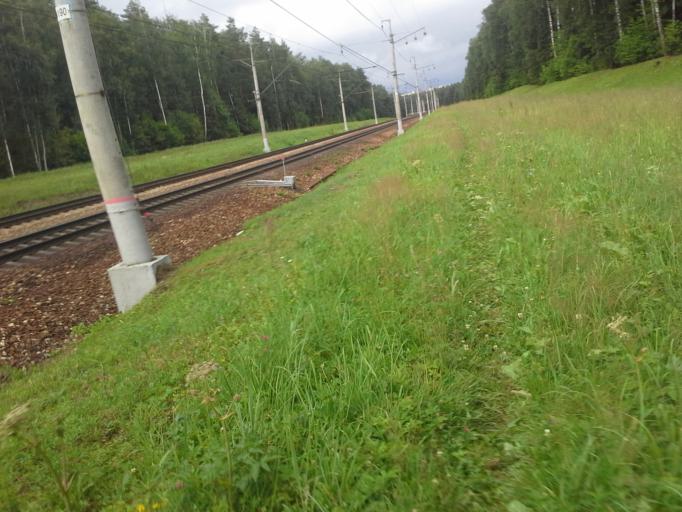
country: RU
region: Moskovskaya
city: Odintsovo
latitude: 55.6475
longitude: 37.2940
